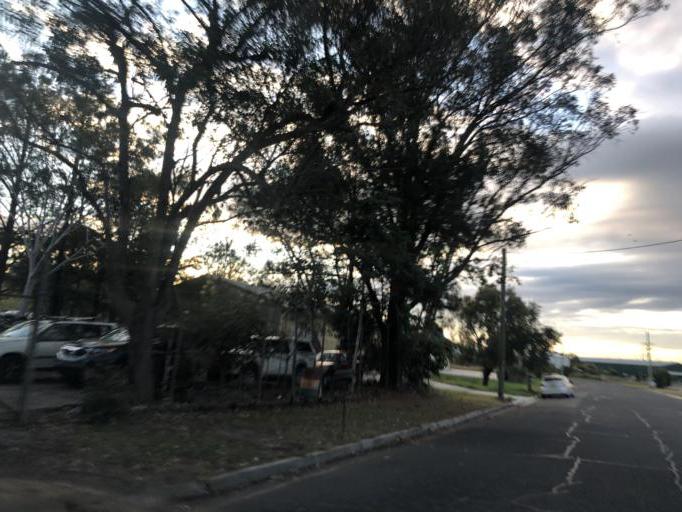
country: AU
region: New South Wales
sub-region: Nambucca Shire
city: Macksville
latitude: -30.7273
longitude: 152.9126
